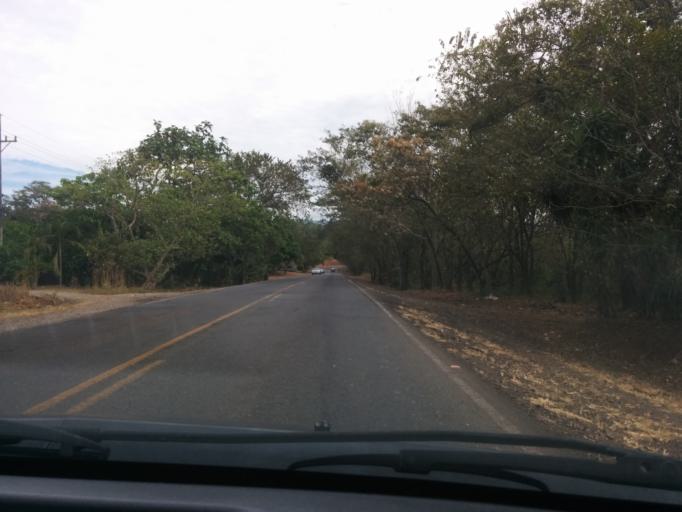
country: CR
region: Puntarenas
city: Esparza
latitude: 10.0044
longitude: -84.6328
